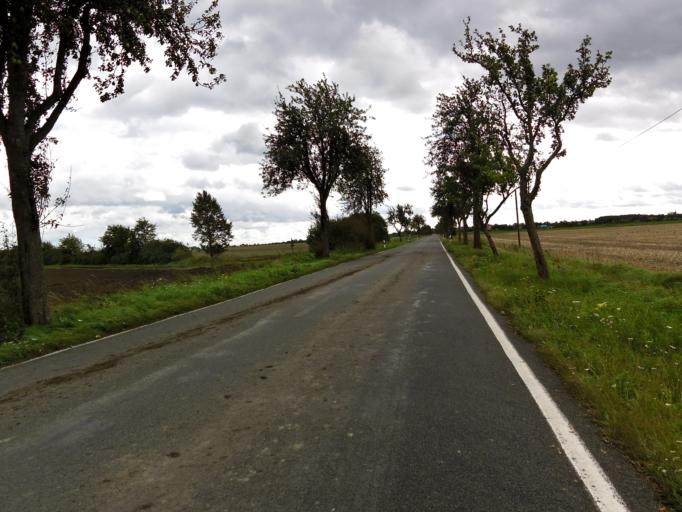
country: DE
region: Saxony-Anhalt
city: Arneburg
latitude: 52.6881
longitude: 11.9911
